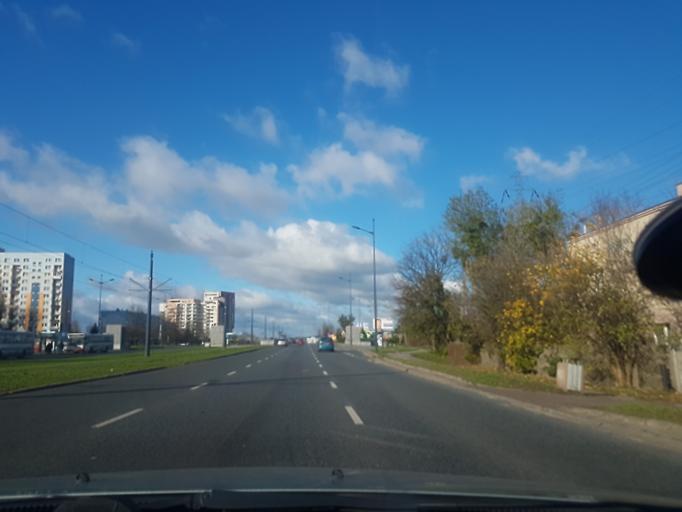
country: PL
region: Lodz Voivodeship
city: Lodz
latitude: 51.7622
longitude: 19.5300
